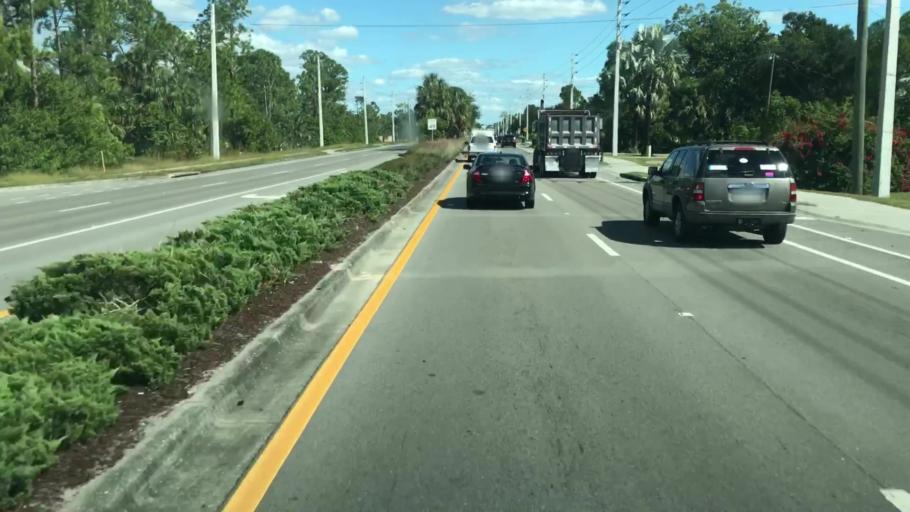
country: US
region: Florida
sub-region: Collier County
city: Golden Gate
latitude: 26.2294
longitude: -81.6366
